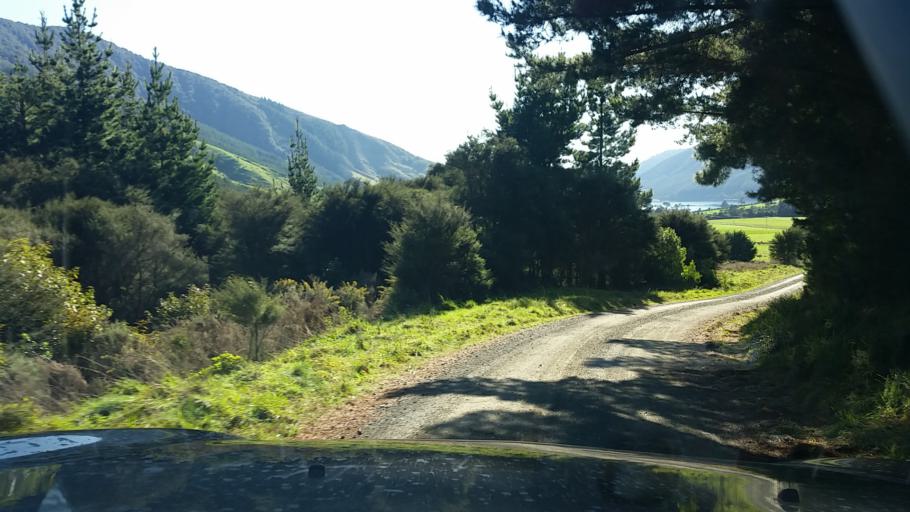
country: NZ
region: Marlborough
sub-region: Marlborough District
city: Picton
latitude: -41.1314
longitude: 174.0392
